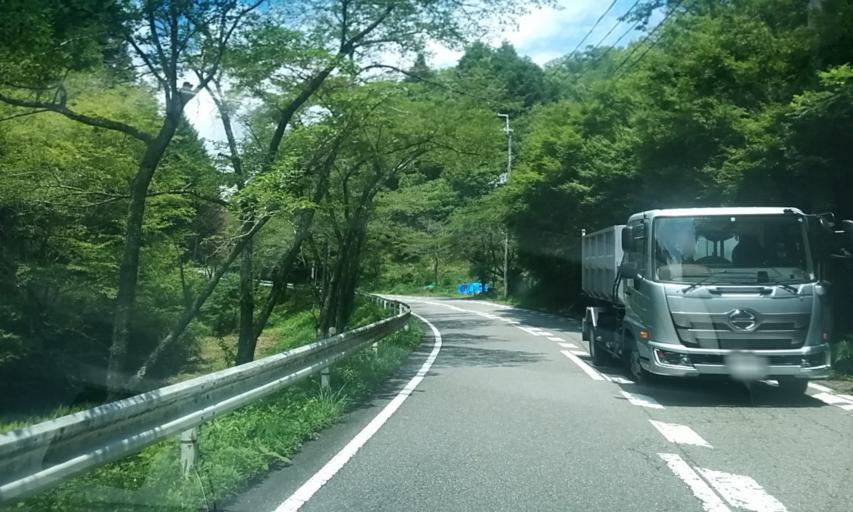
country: JP
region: Hyogo
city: Sasayama
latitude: 35.1724
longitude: 135.2490
